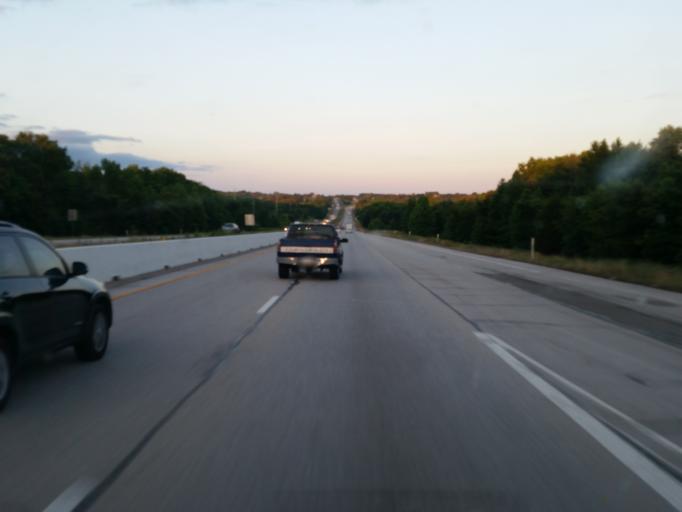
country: US
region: Texas
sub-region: Smith County
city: Hideaway
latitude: 32.4831
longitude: -95.5188
